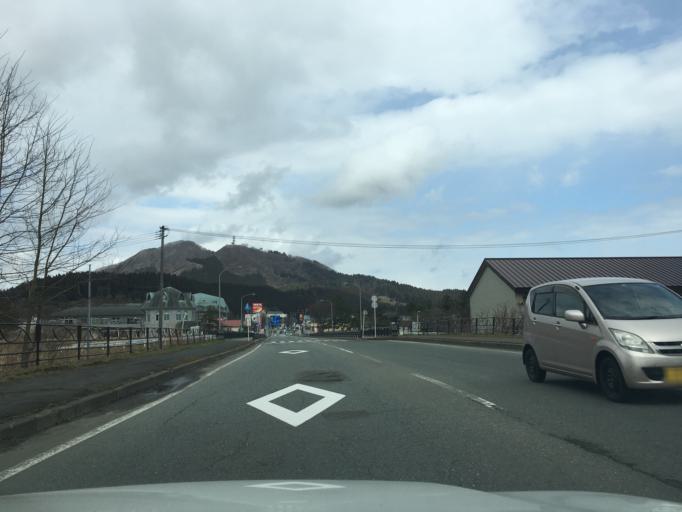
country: JP
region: Akita
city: Tenno
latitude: 39.9401
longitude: 140.1120
